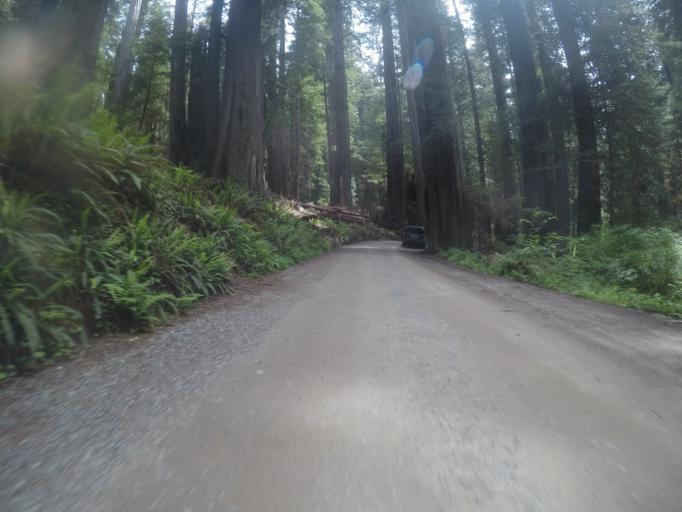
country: US
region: California
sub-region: Del Norte County
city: Bertsch-Oceanview
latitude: 41.7664
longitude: -124.1163
